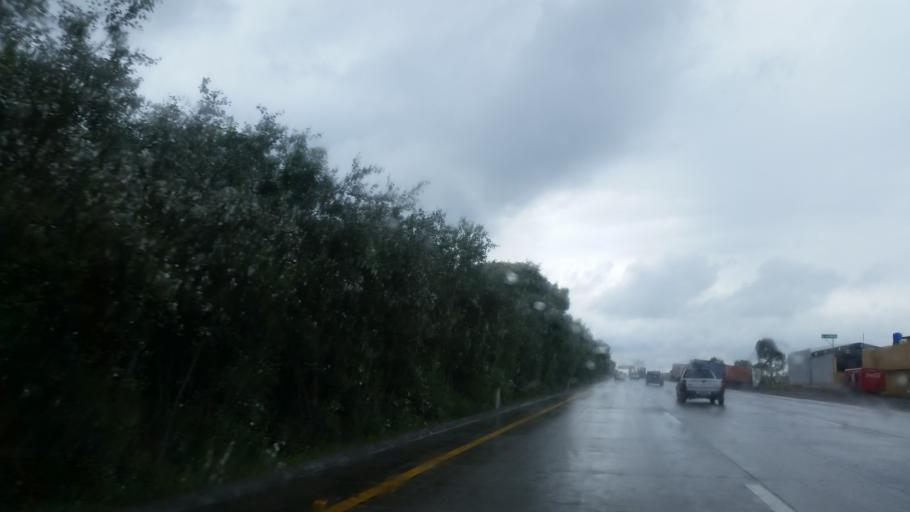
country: MX
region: Mexico
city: San Francisco Soyaniquilpan
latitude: 19.9883
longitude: -99.4534
